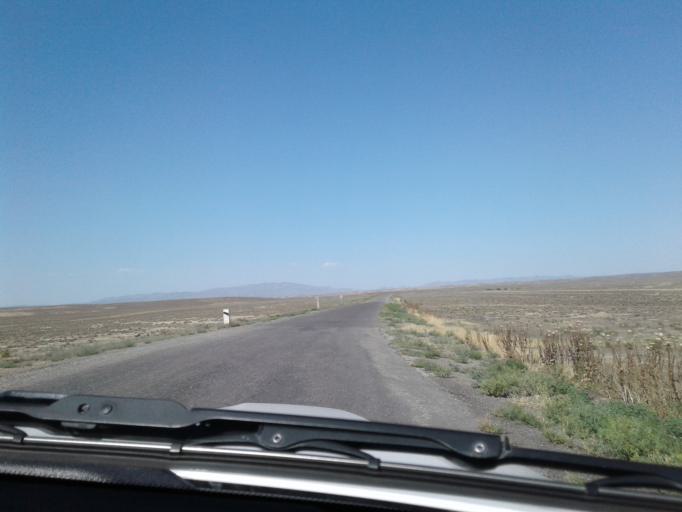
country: TM
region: Balkan
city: Magtymguly
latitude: 38.6026
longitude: 56.1974
